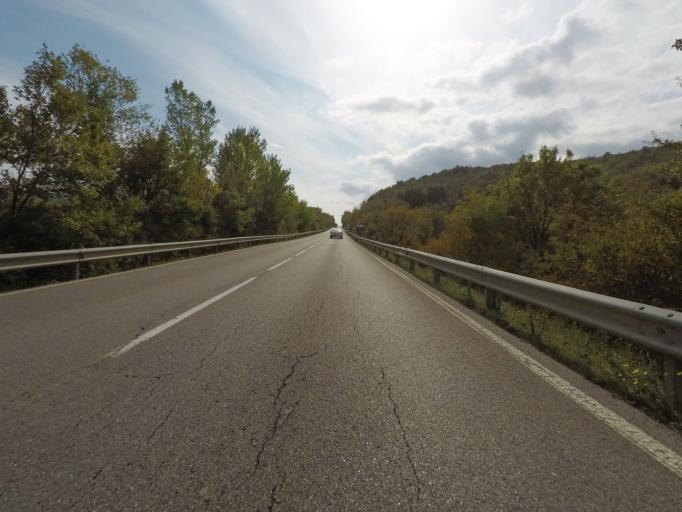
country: IT
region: Tuscany
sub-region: Provincia di Siena
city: Murlo
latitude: 43.1439
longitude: 11.2872
